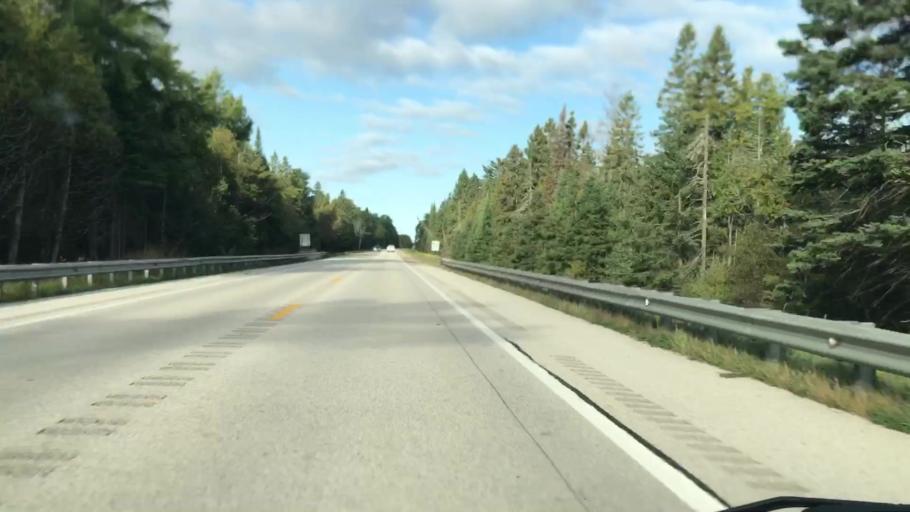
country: US
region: Michigan
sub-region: Luce County
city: Newberry
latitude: 46.3319
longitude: -85.0778
